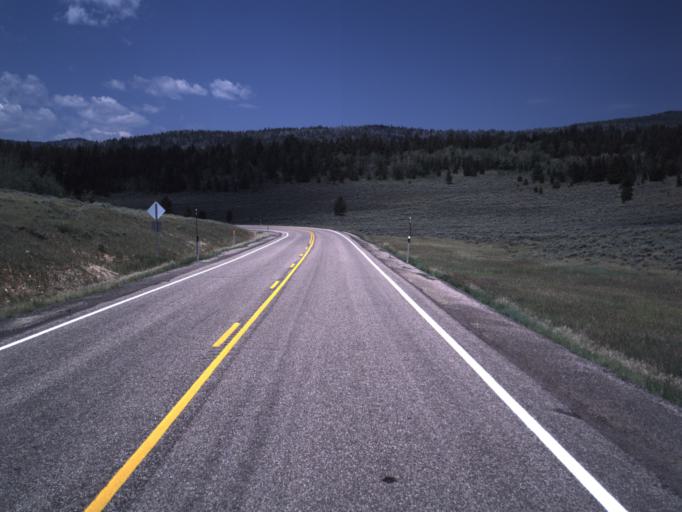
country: US
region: Utah
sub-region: Uintah County
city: Maeser
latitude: 40.7152
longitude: -109.4828
